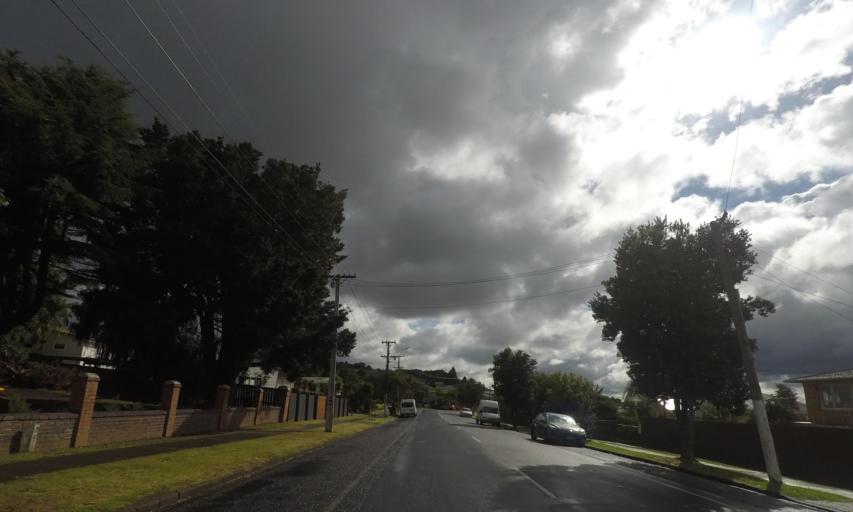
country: NZ
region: Auckland
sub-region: Auckland
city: Mangere
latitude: -36.9521
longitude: 174.7865
